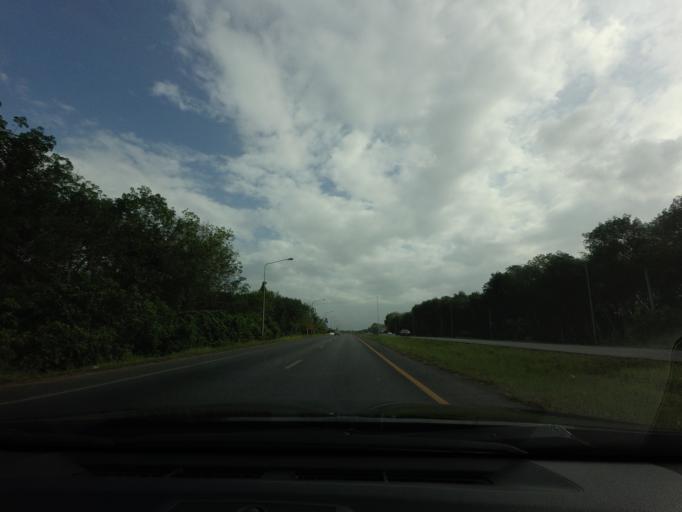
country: TH
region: Yala
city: Yala
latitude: 6.5736
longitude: 101.2612
